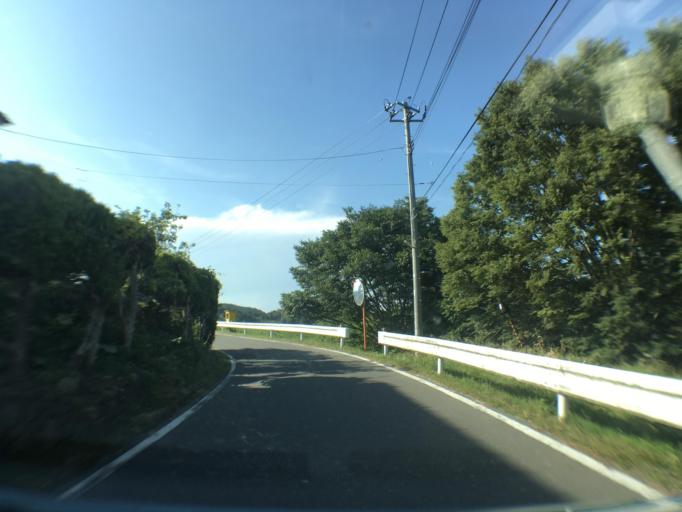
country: JP
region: Miyagi
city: Wakuya
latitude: 38.6126
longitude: 141.2943
